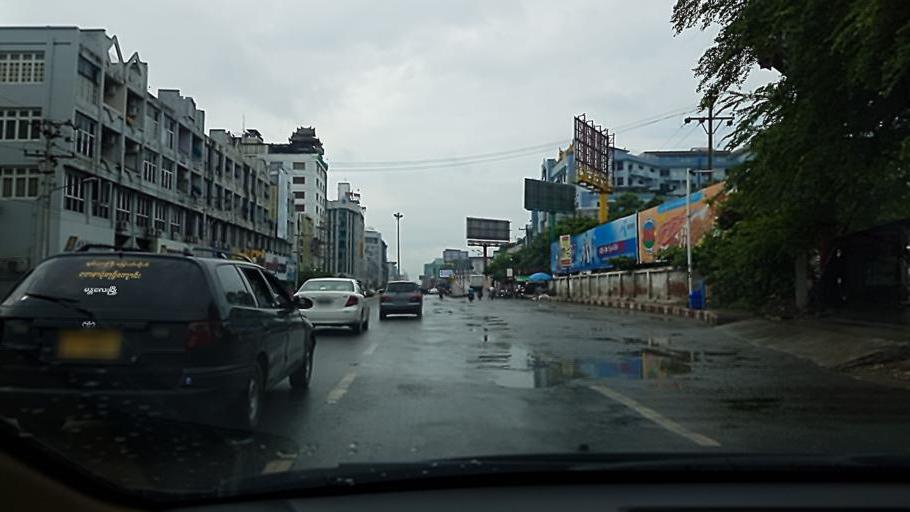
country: MM
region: Mandalay
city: Mandalay
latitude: 21.9786
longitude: 96.0870
